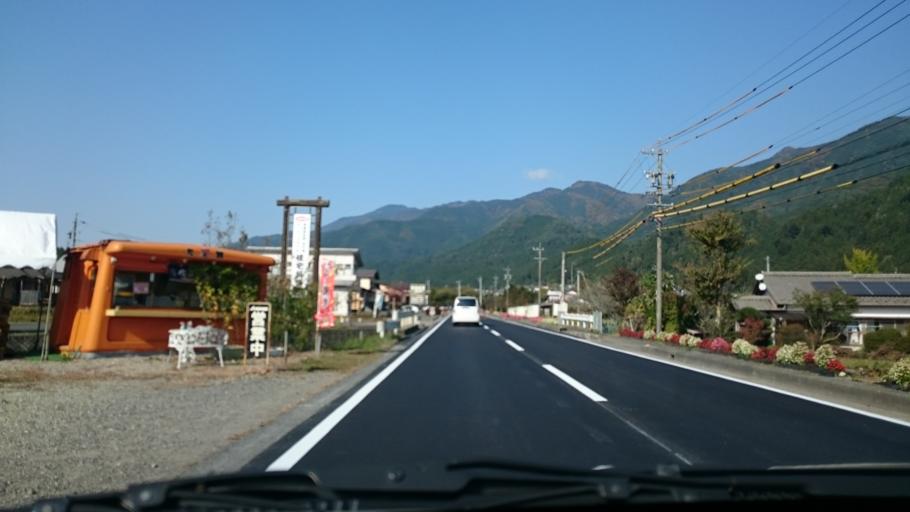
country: JP
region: Gifu
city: Nakatsugawa
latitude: 35.6970
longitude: 137.3808
